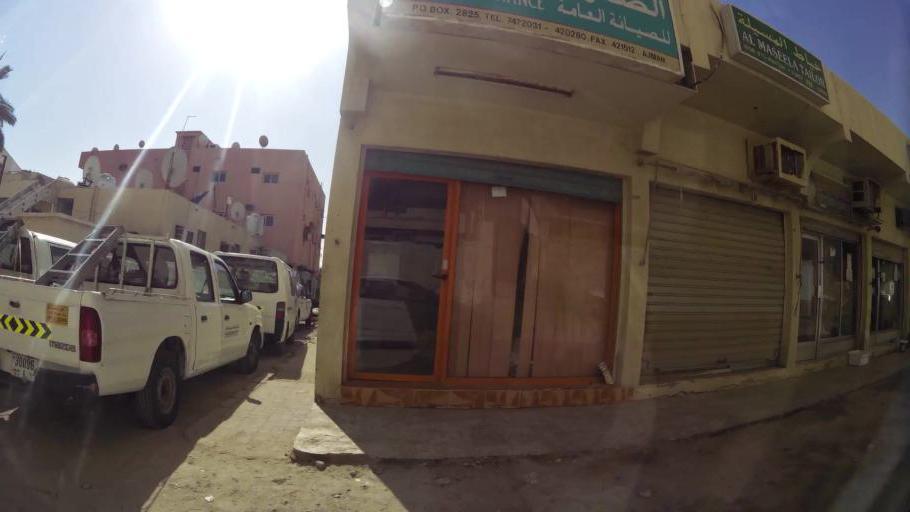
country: AE
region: Ajman
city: Ajman
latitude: 25.4144
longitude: 55.4471
